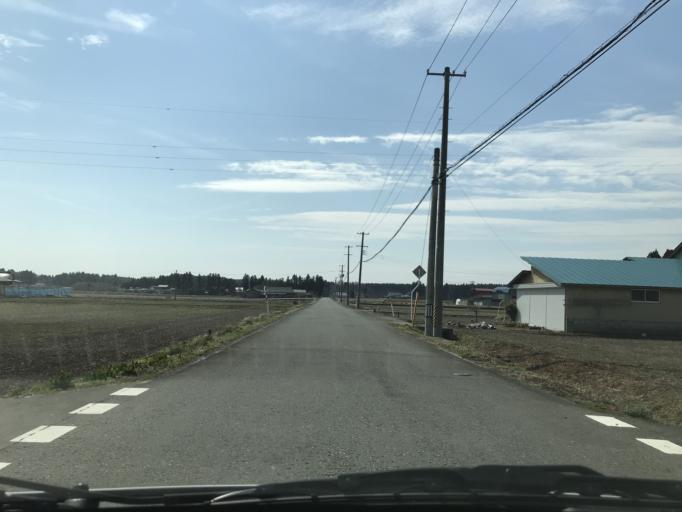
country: JP
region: Iwate
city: Mizusawa
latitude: 39.1275
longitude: 141.0435
